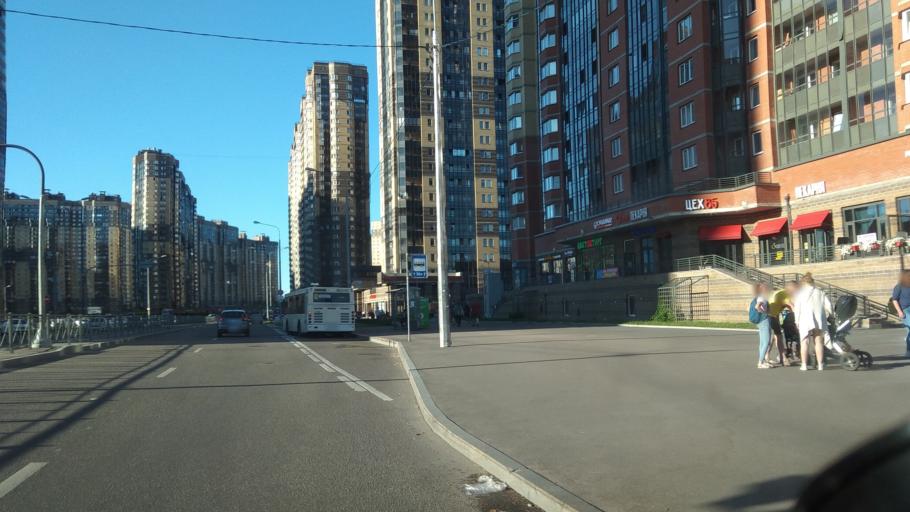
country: RU
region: Leningrad
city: Parnas
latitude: 60.0761
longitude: 30.3421
